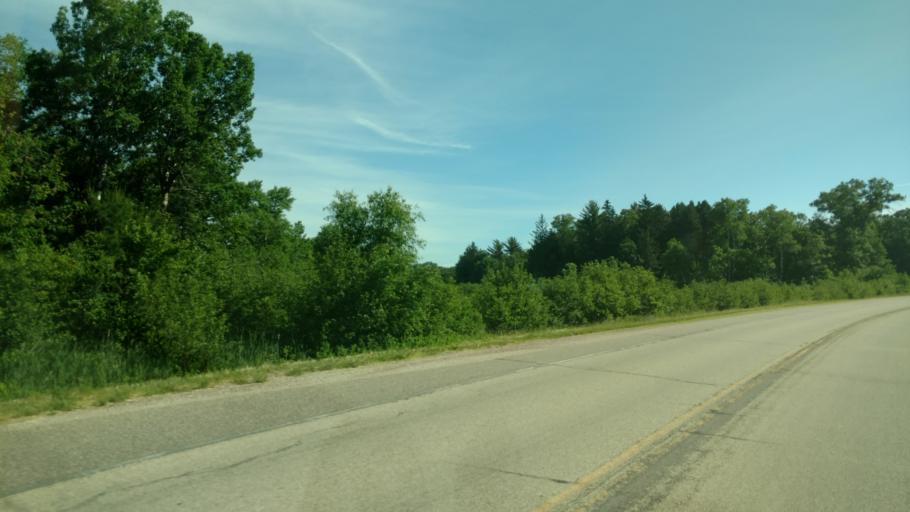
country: US
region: Wisconsin
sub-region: Sauk County
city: Lake Delton
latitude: 43.5676
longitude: -89.8364
